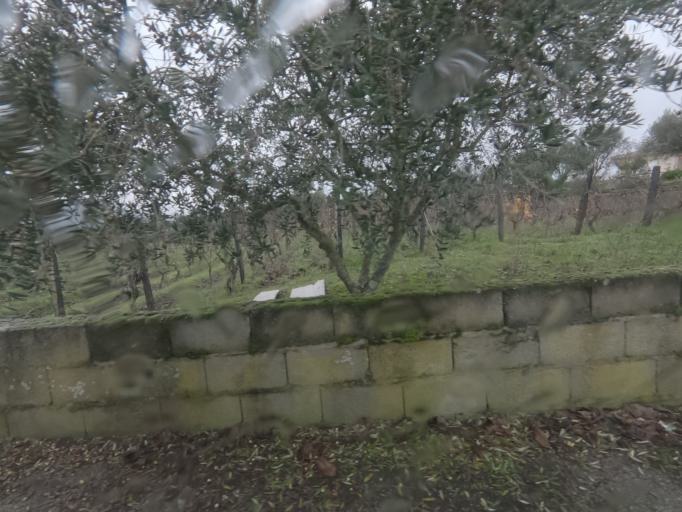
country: PT
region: Viseu
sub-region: Armamar
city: Armamar
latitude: 41.1670
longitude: -7.7157
